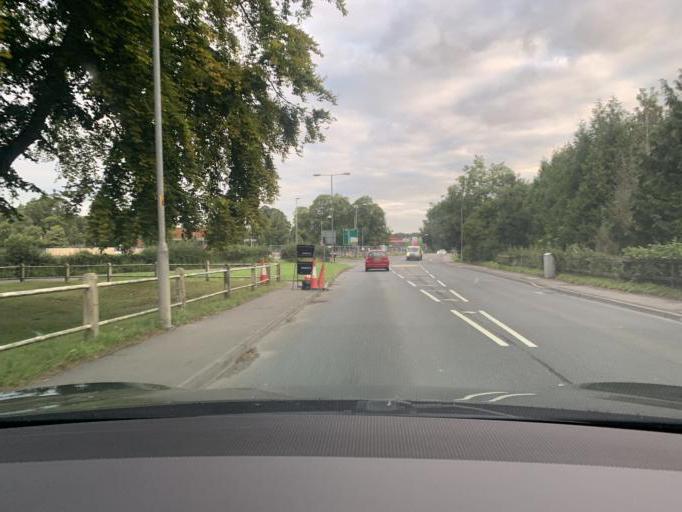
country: GB
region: England
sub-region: Wiltshire
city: Tidworth
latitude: 51.2368
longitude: -1.6641
